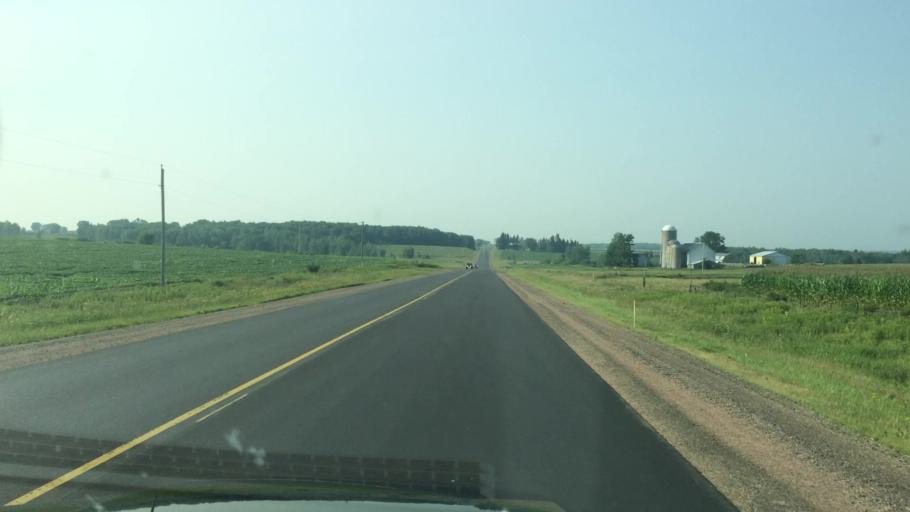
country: US
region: Wisconsin
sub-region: Marathon County
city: Athens
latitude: 44.9189
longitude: -90.0786
